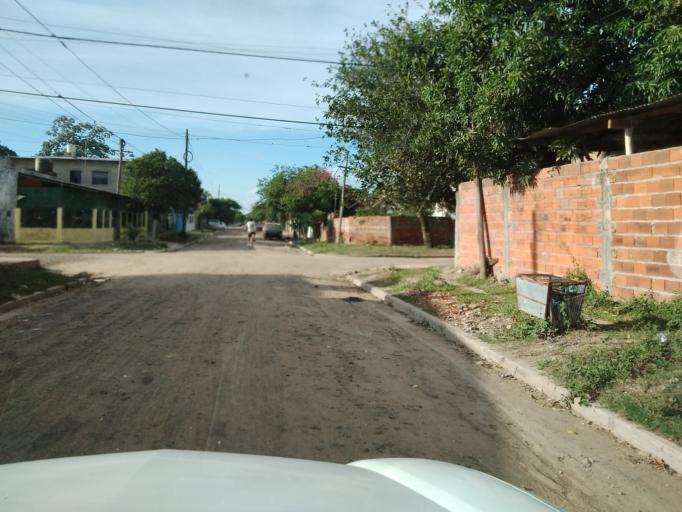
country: AR
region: Corrientes
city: Corrientes
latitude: -27.4919
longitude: -58.8454
